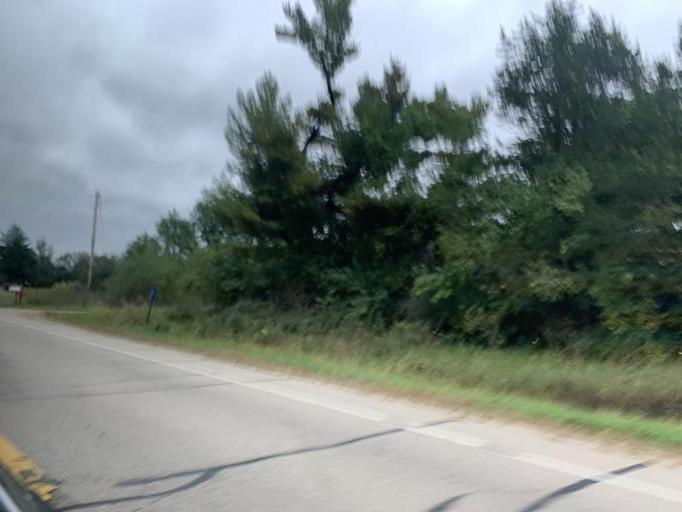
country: US
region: Wisconsin
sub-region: Grant County
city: Boscobel
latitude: 43.2054
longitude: -90.6077
